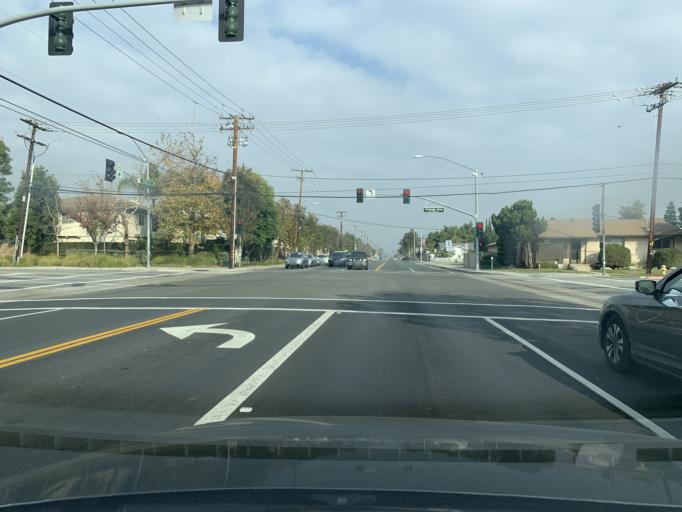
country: US
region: California
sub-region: Orange County
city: Cypress
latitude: 33.8241
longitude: -118.0369
